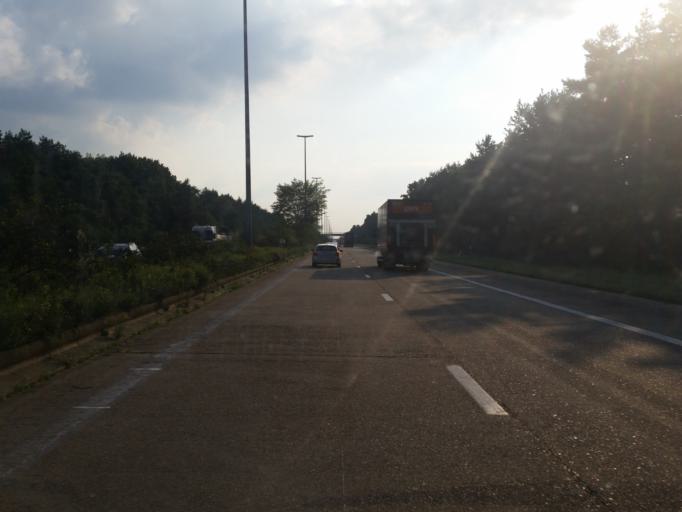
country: BE
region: Flanders
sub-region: Provincie Antwerpen
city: Lille
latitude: 51.2740
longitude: 4.8345
